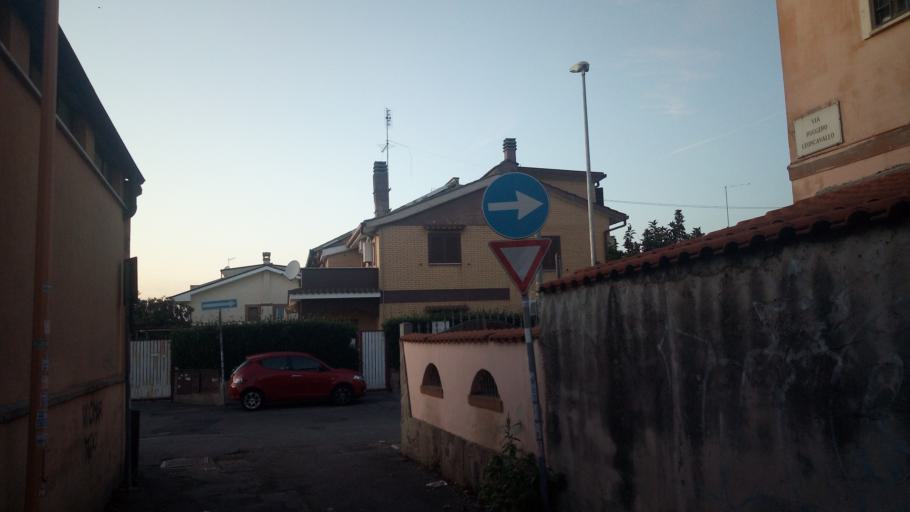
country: IT
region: Latium
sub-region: Citta metropolitana di Roma Capitale
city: Ciampino
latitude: 41.8064
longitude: 12.5950
